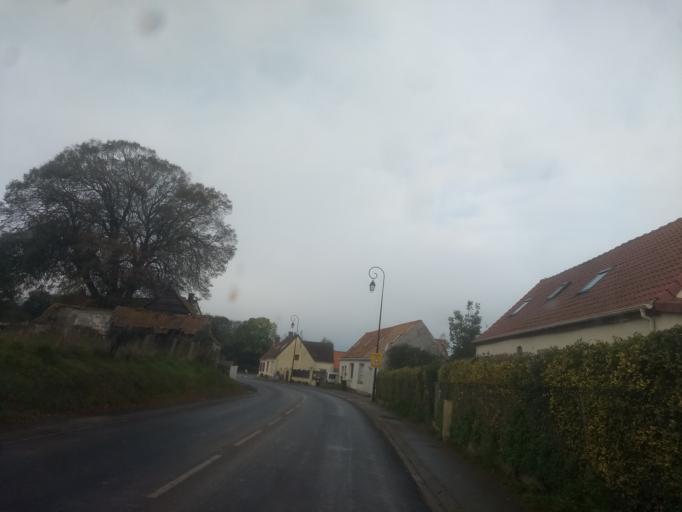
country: FR
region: Nord-Pas-de-Calais
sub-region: Departement du Pas-de-Calais
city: Wissant
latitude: 50.8817
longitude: 1.7159
